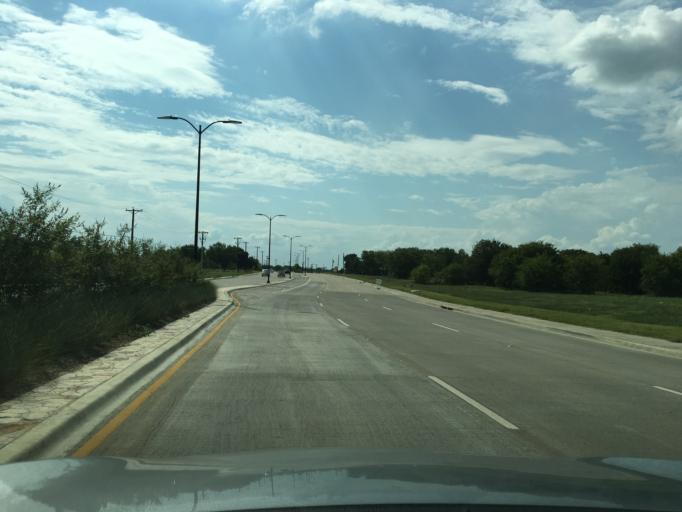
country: US
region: Texas
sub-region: Denton County
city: Oak Point
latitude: 33.1659
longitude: -96.9706
